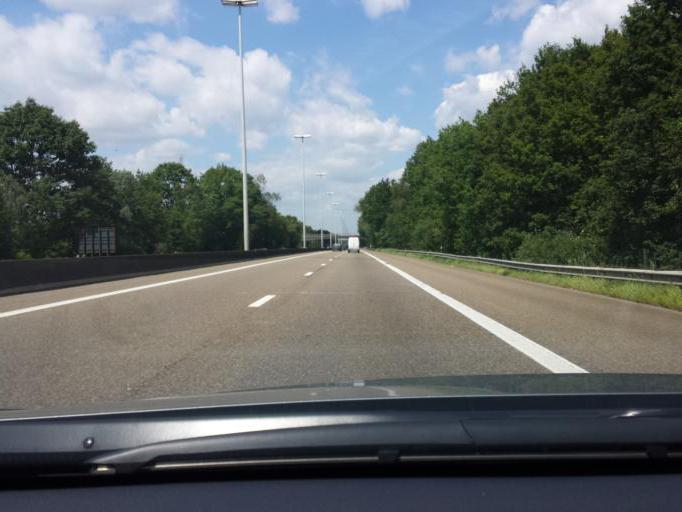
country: BE
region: Flanders
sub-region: Provincie Limburg
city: Hasselt
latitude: 50.9576
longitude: 5.2698
